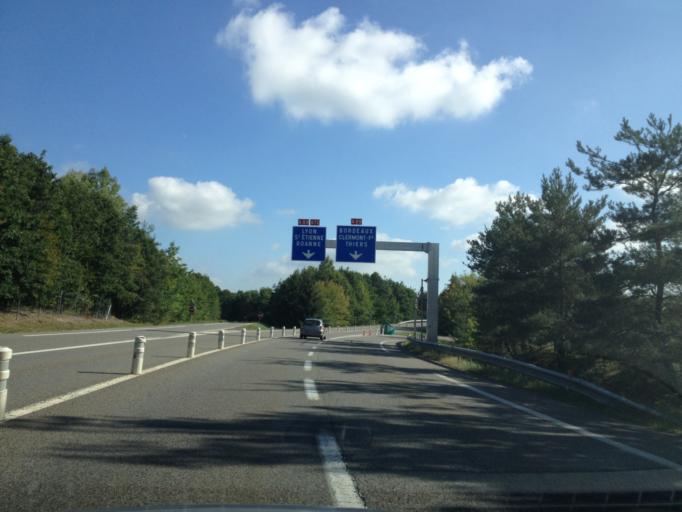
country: FR
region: Rhone-Alpes
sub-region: Departement de la Loire
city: Saint-Germain-Laval
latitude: 45.8593
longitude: 4.0441
